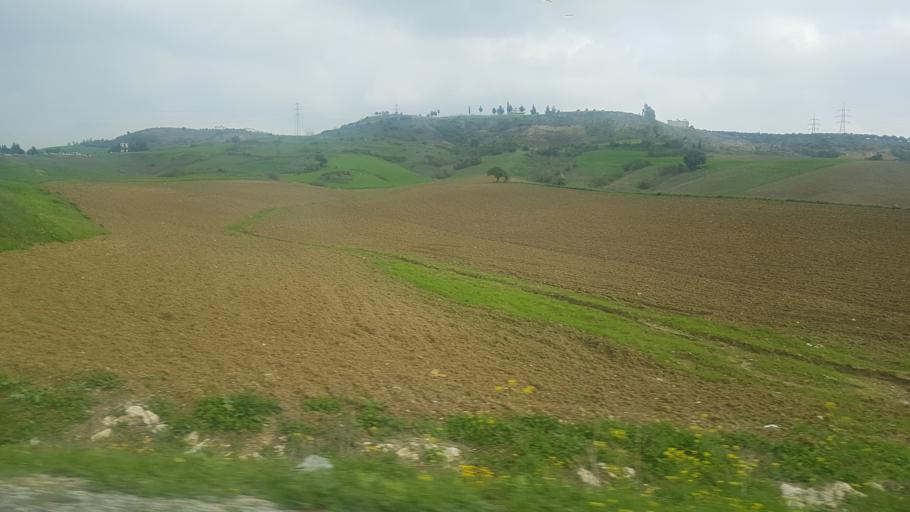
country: TR
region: Mersin
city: Yenice
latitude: 37.0619
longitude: 35.1698
